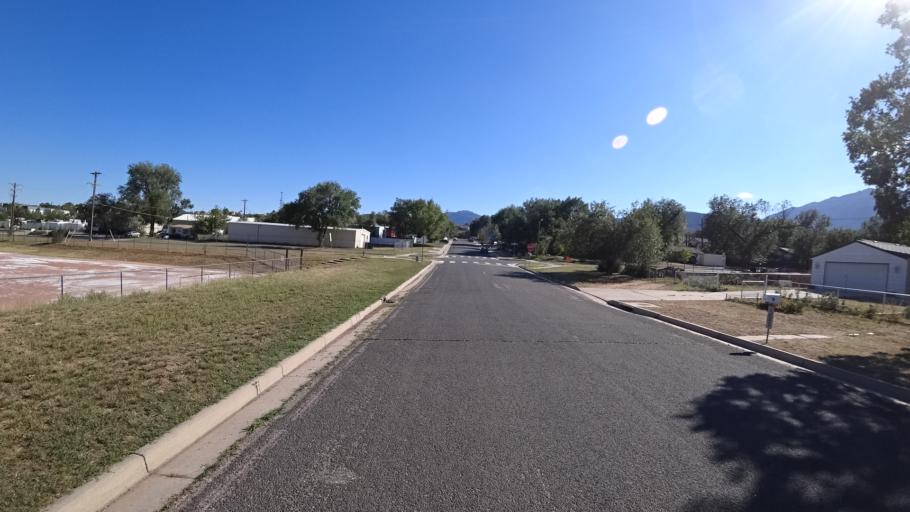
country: US
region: Colorado
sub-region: El Paso County
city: Colorado Springs
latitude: 38.8378
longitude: -104.8643
